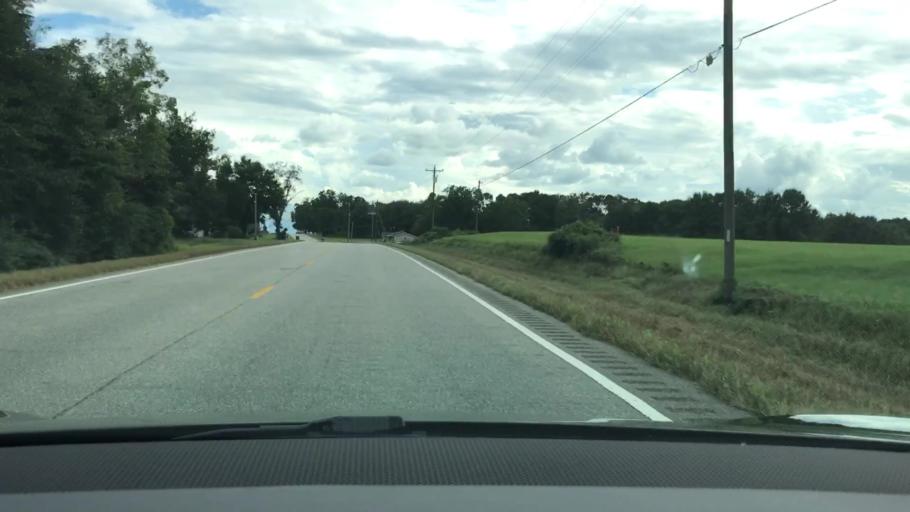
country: US
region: Alabama
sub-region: Pike County
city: Troy
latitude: 31.6691
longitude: -85.9590
